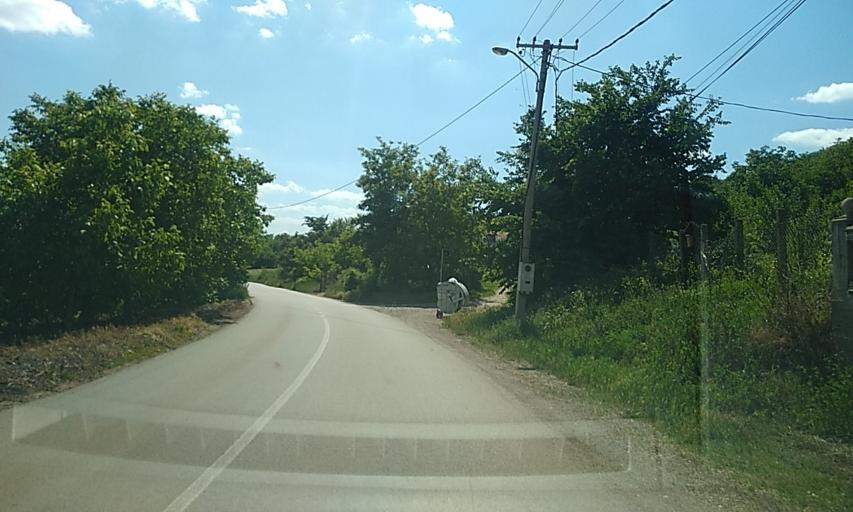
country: RS
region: Central Serbia
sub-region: Nisavski Okrug
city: Niska Banja
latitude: 43.3691
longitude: 21.9856
